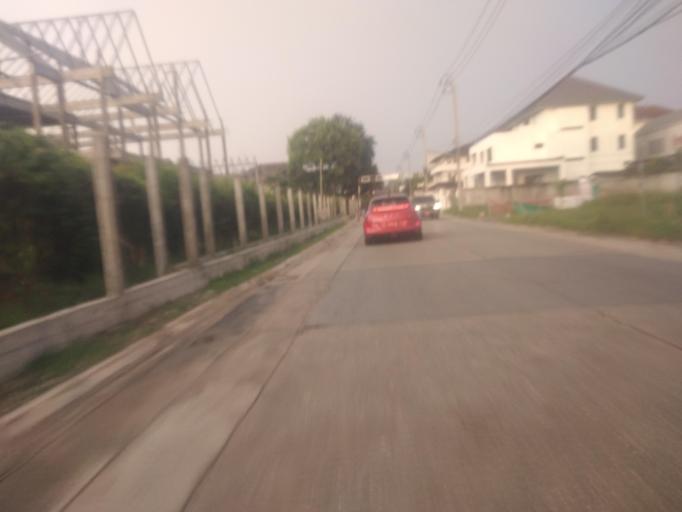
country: TH
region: Bangkok
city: Phasi Charoen
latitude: 13.7423
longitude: 100.4438
